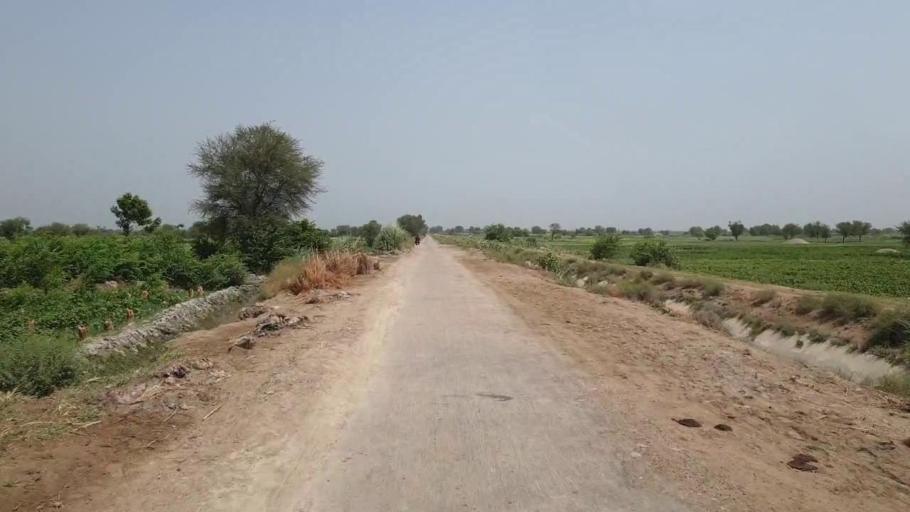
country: PK
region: Sindh
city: Nawabshah
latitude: 26.2732
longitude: 68.3146
